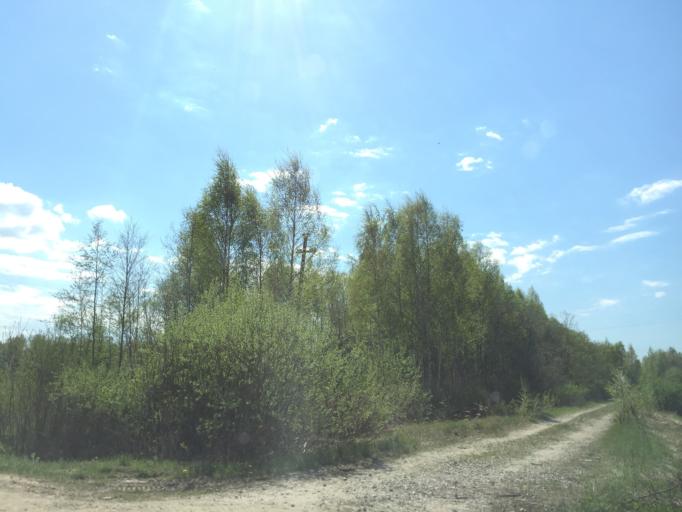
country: LV
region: Saulkrastu
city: Saulkrasti
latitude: 57.3583
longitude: 24.5026
